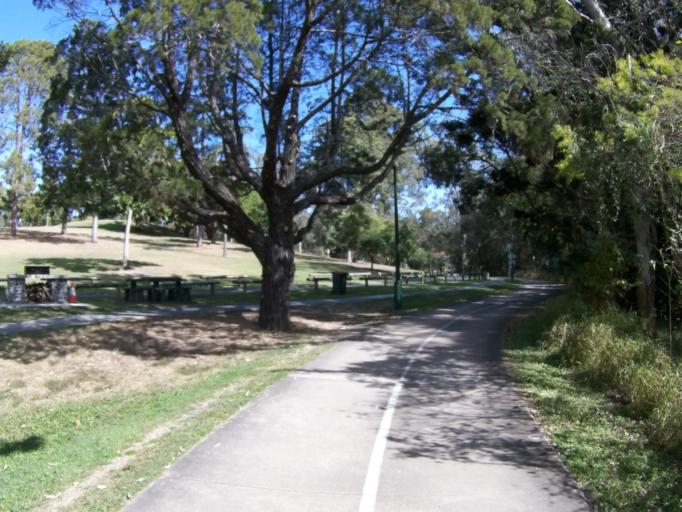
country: AU
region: Queensland
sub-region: Brisbane
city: Toowong
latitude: -27.4788
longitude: 152.9817
